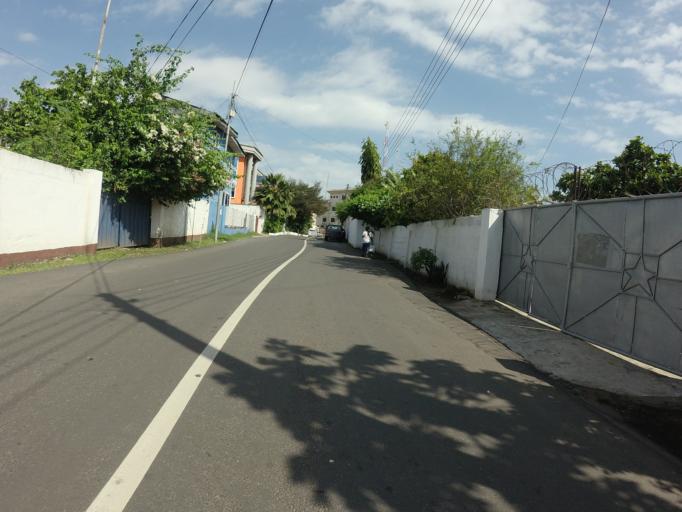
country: GH
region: Greater Accra
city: Accra
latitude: 5.5737
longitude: -0.2029
